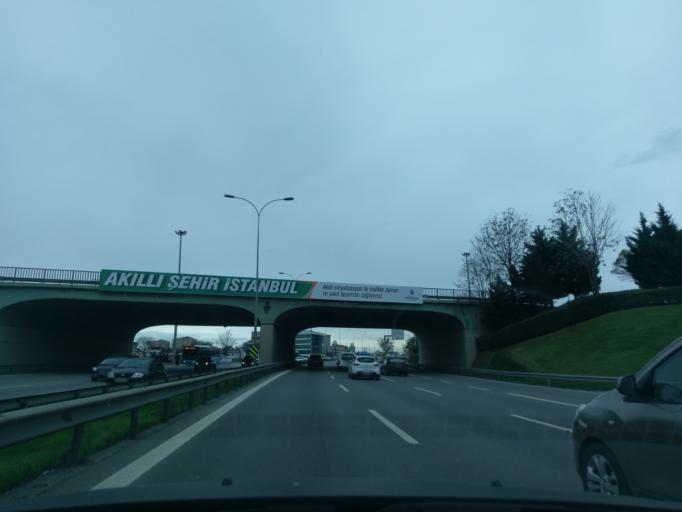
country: TR
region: Istanbul
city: Maltepe
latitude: 40.9249
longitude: 29.1529
